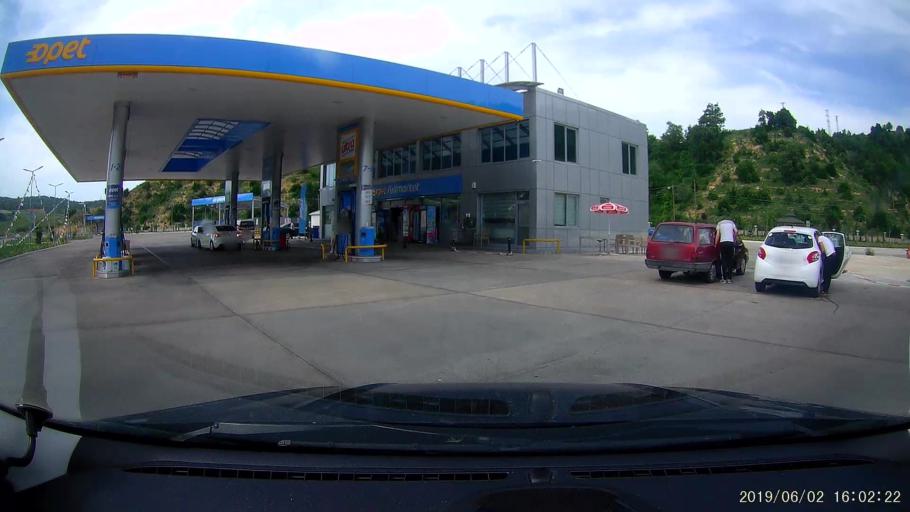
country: TR
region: Samsun
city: Havza
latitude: 40.9419
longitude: 35.6585
